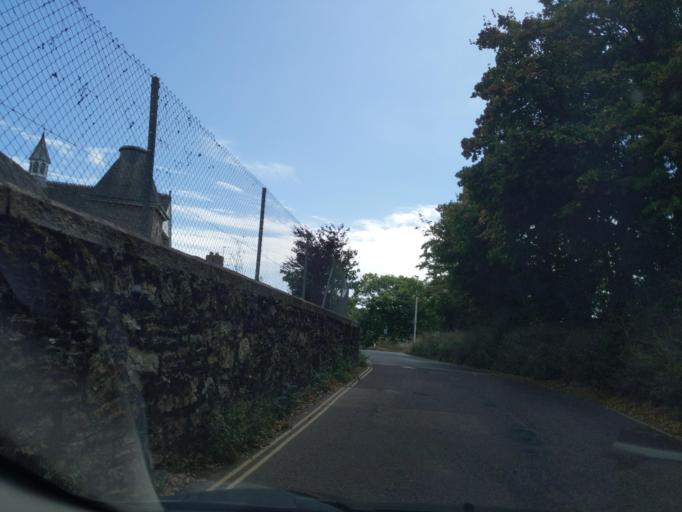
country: GB
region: England
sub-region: Devon
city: Modbury
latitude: 50.3506
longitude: -3.8897
